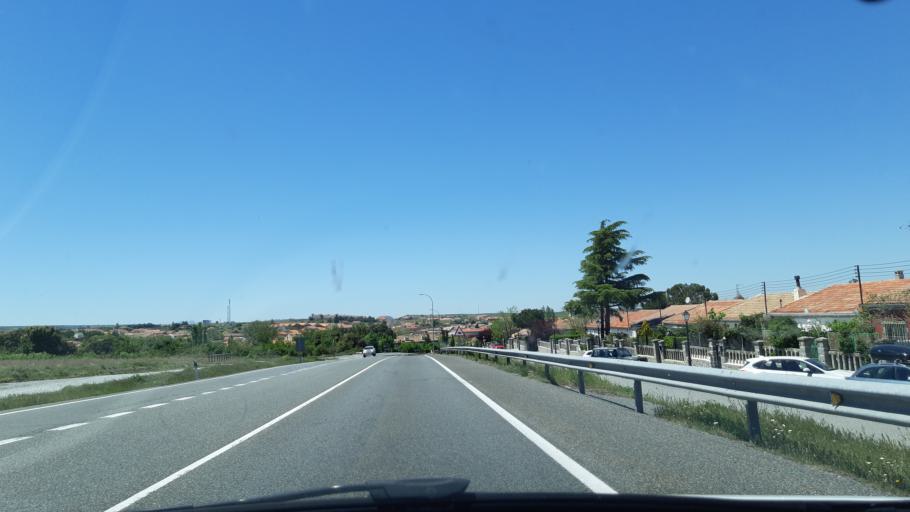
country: ES
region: Castille and Leon
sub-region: Provincia de Segovia
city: Villacastin
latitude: 40.7781
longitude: -4.4033
